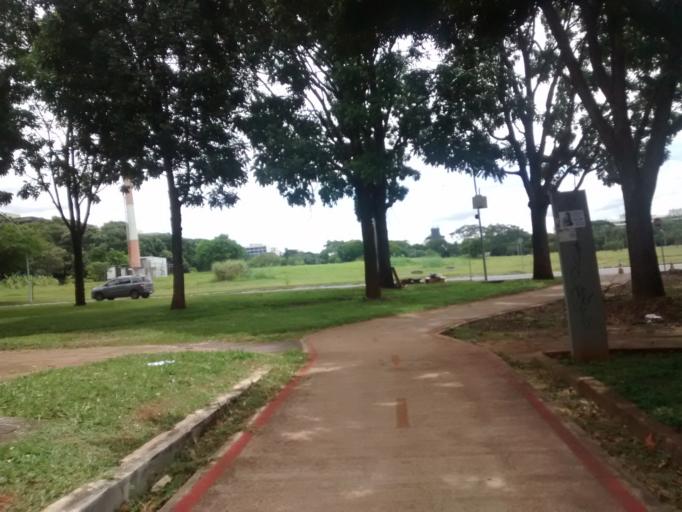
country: BR
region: Federal District
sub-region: Brasilia
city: Brasilia
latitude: -15.7662
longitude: -47.8788
